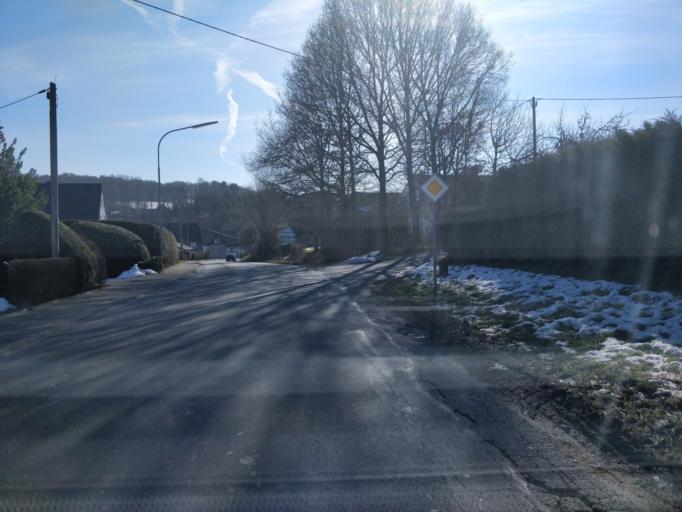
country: DE
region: North Rhine-Westphalia
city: Wiehl
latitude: 50.9285
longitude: 7.5525
